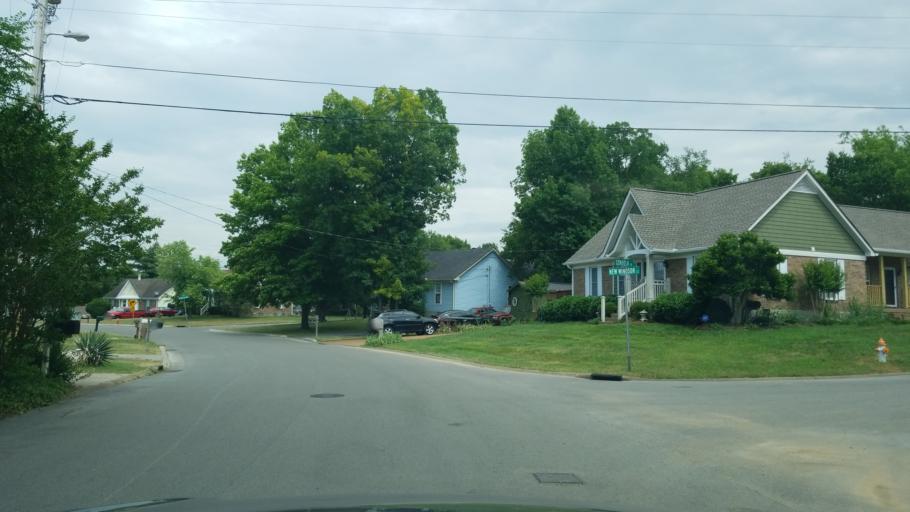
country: US
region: Tennessee
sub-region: Rutherford County
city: La Vergne
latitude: 36.0827
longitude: -86.6002
